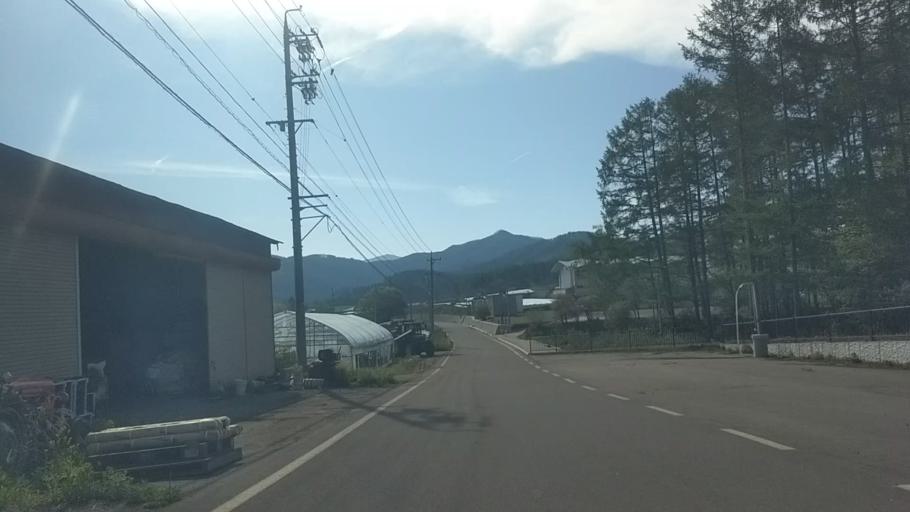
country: JP
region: Yamanashi
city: Nirasaki
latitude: 35.9369
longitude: 138.4656
